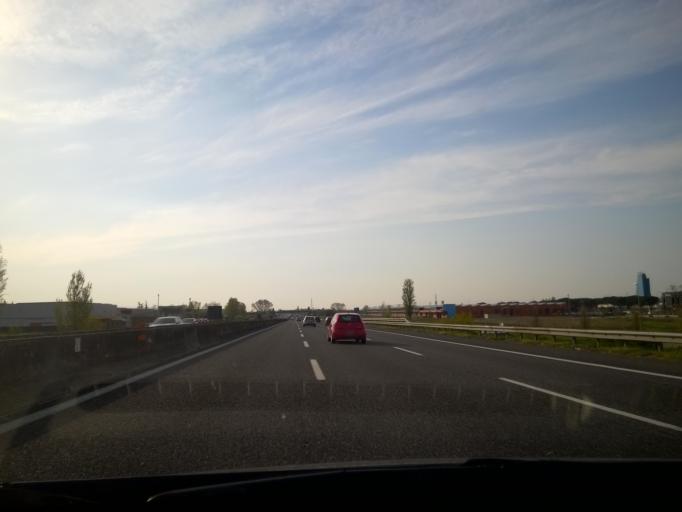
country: IT
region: Emilia-Romagna
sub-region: Forli-Cesena
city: Forli
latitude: 44.2541
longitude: 12.0859
